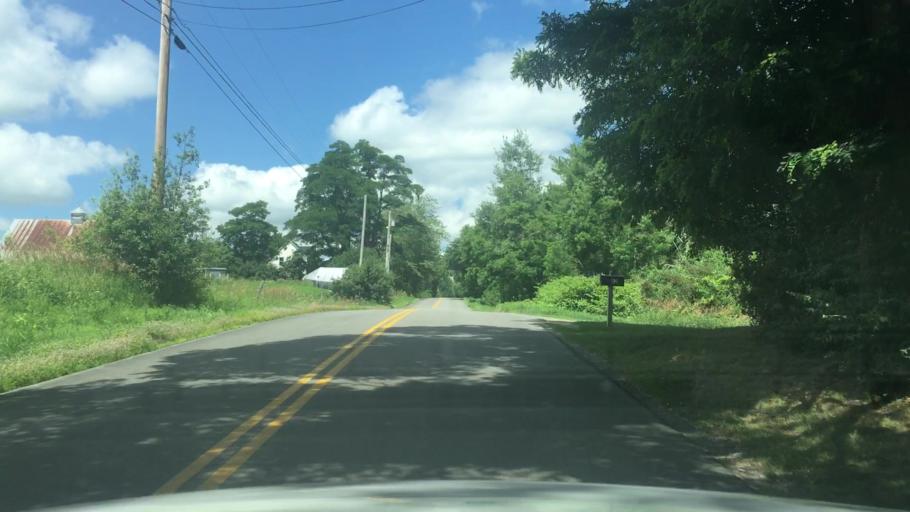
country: US
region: Maine
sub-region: Waldo County
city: Belfast
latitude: 44.4104
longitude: -69.0366
